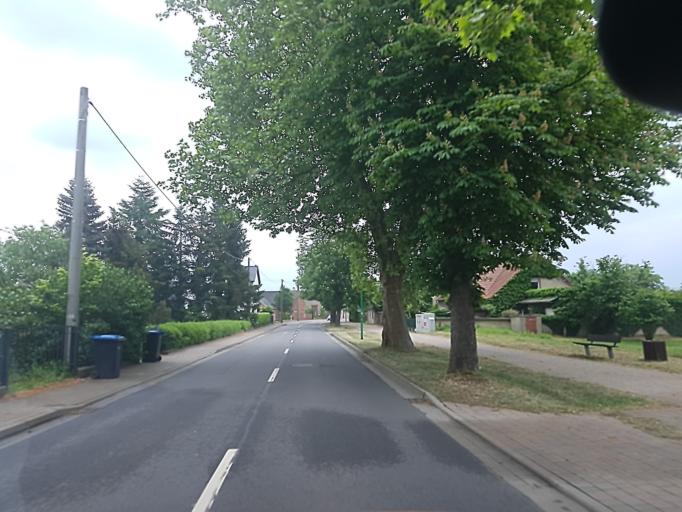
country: DE
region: Saxony-Anhalt
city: Jessen
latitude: 51.7955
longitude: 13.0205
